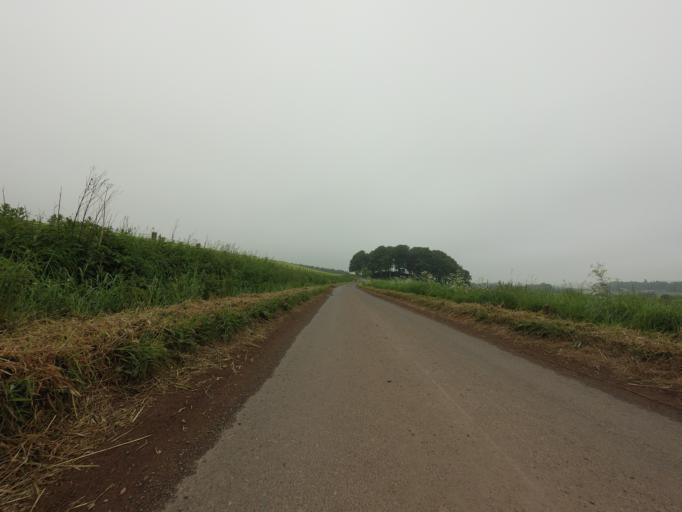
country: GB
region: Scotland
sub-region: Fife
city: Auchtermuchty
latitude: 56.2699
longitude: -3.2889
